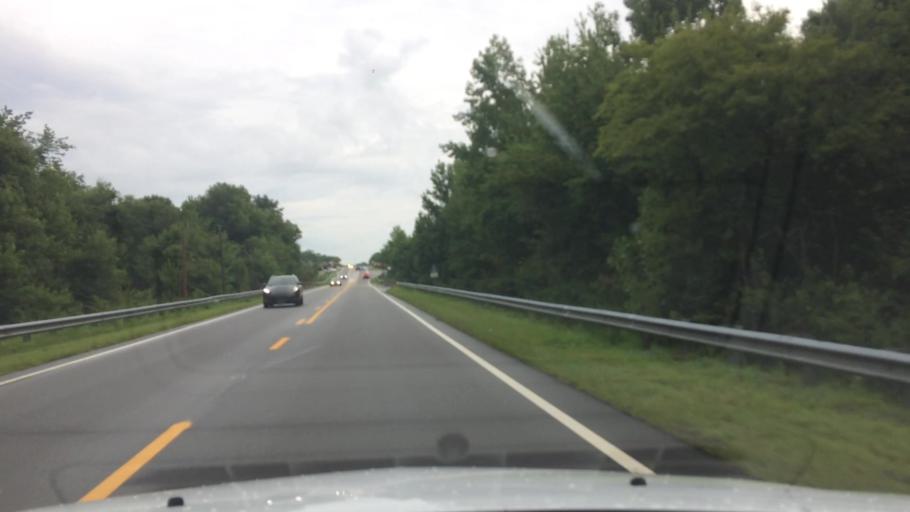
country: US
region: North Carolina
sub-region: Pitt County
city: Farmville
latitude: 35.5946
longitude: -77.5581
